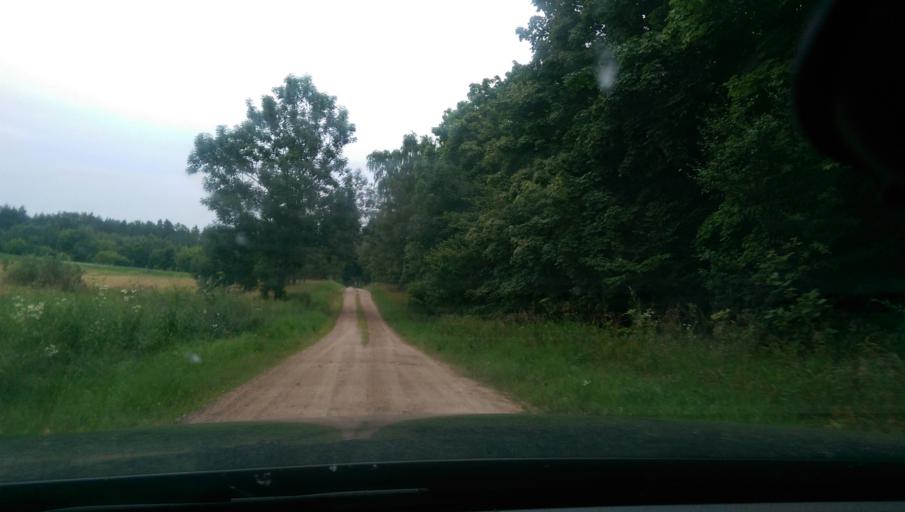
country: PL
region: Warmian-Masurian Voivodeship
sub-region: Powiat piski
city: Orzysz
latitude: 53.8226
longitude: 21.8103
